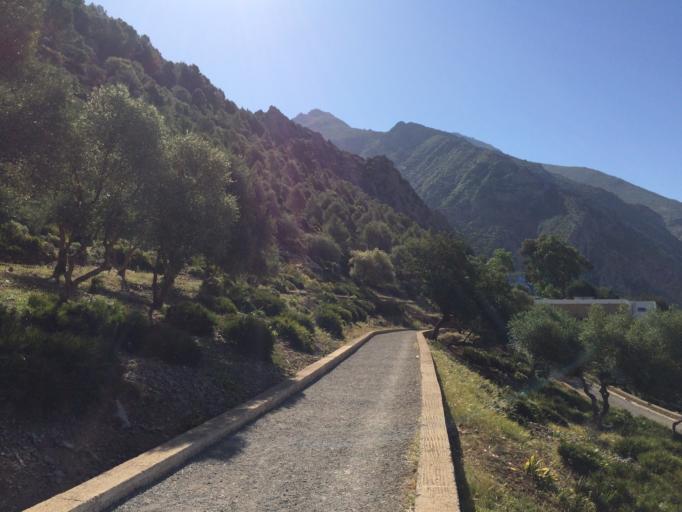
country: MA
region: Tanger-Tetouan
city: Chefchaouene
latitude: 35.1739
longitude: -5.2626
